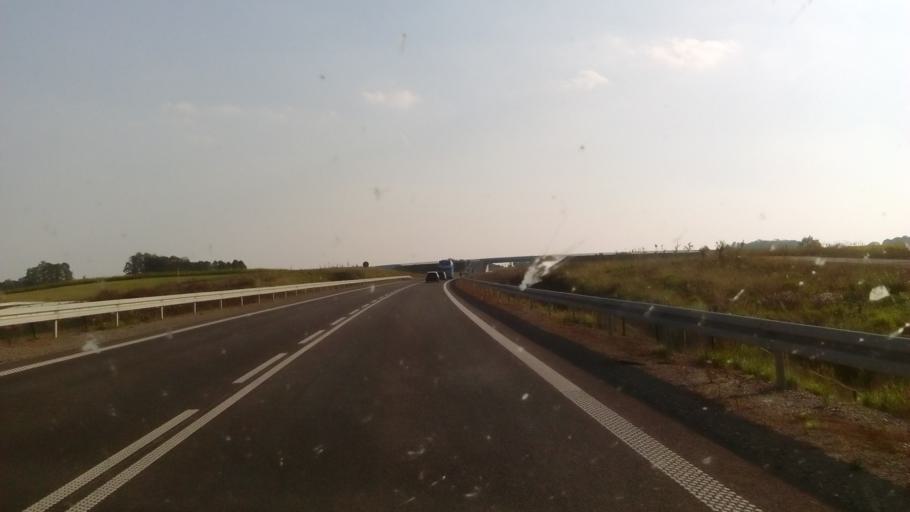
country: PL
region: Podlasie
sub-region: Powiat grajewski
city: Rajgrod
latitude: 53.7691
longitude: 22.8328
